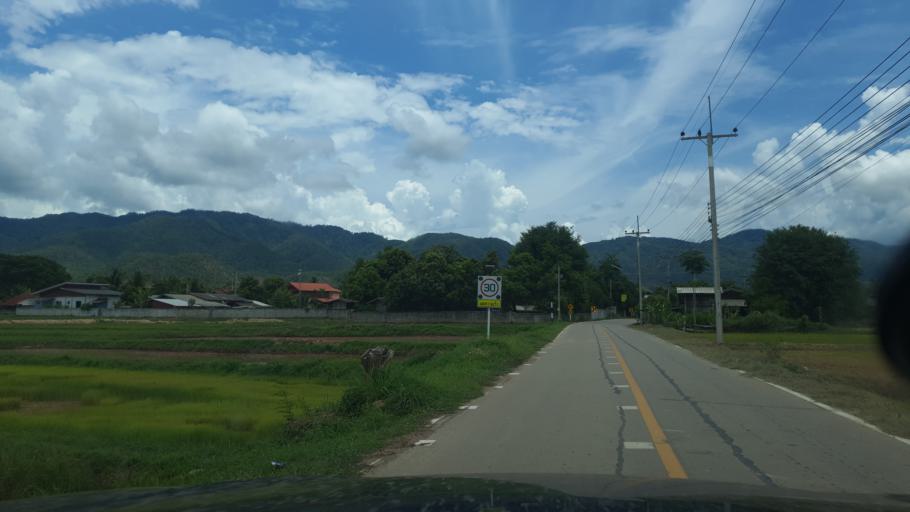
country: TH
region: Lampang
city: Sop Prap
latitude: 17.9099
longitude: 99.4135
